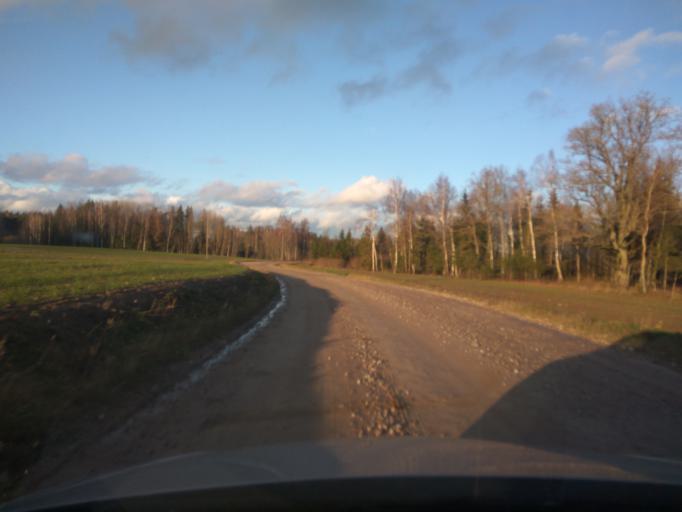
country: LV
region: Aizpute
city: Aizpute
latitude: 56.7821
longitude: 21.7918
